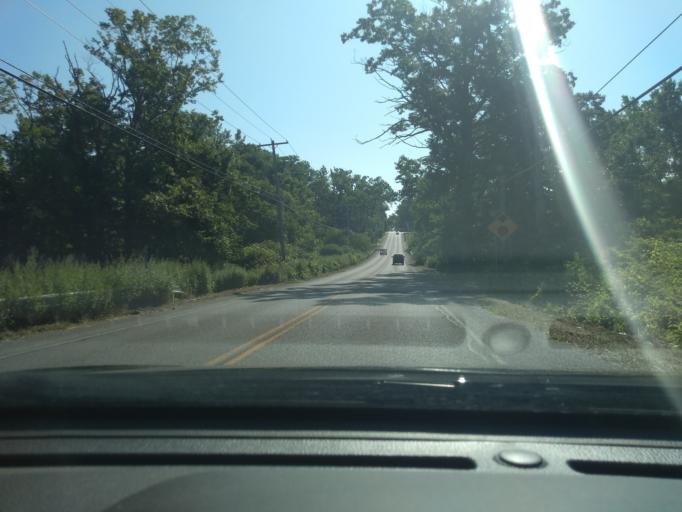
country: US
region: New York
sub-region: Erie County
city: Orchard Park
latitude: 42.7891
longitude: -78.7304
